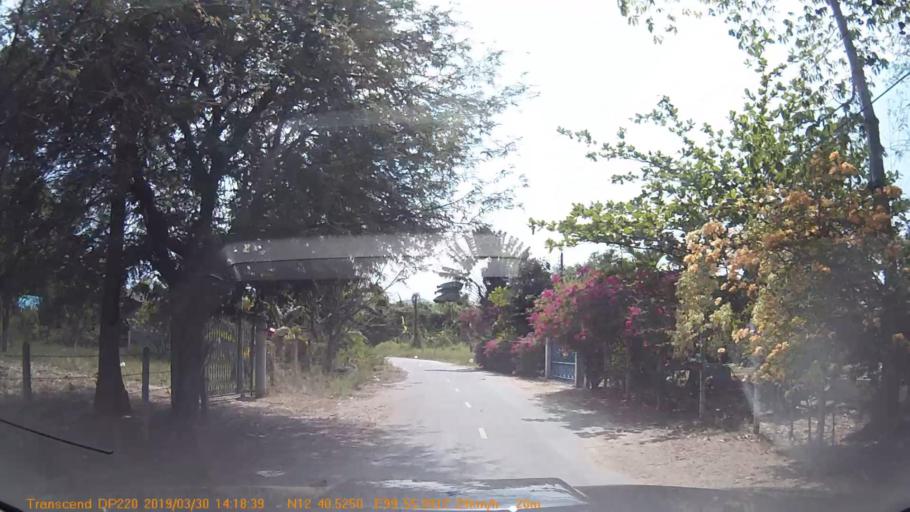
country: TH
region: Prachuap Khiri Khan
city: Hua Hin
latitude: 12.6753
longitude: 99.9331
